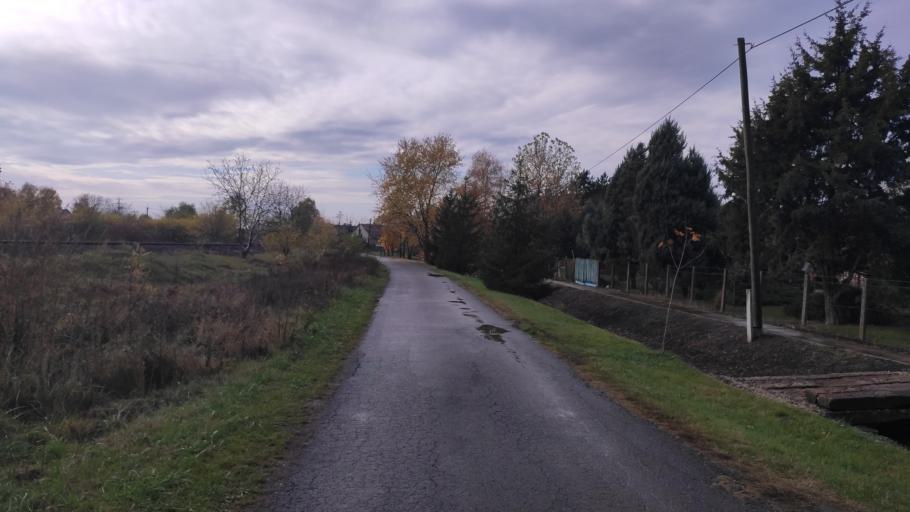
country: HU
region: Bekes
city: Mezobereny
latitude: 46.7640
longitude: 21.0396
